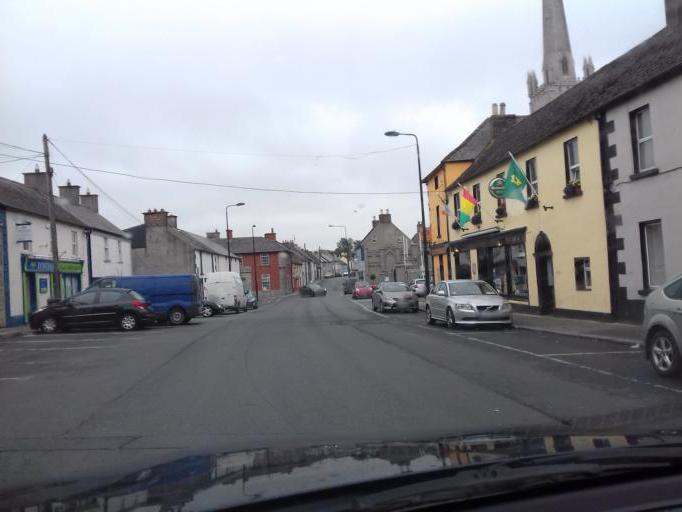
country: IE
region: Leinster
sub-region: County Carlow
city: Bagenalstown
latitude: 52.7021
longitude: -6.9572
